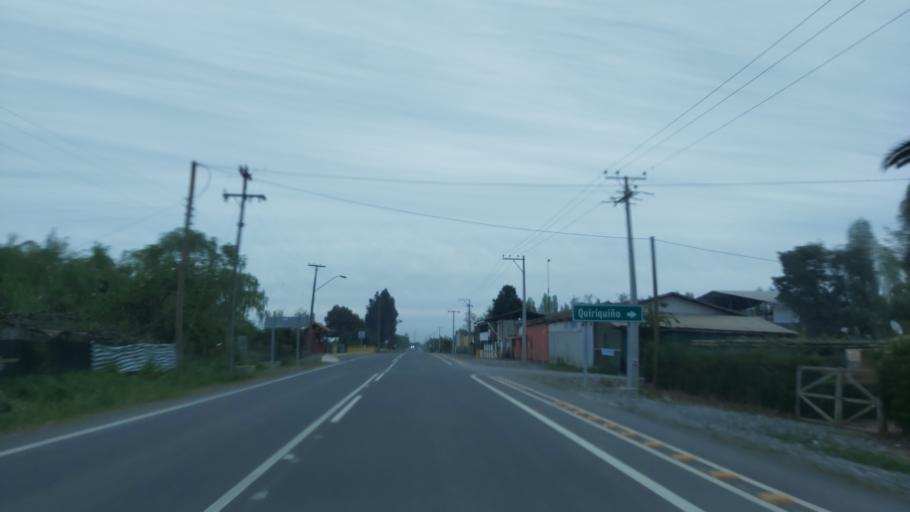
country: CL
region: Maule
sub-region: Provincia de Linares
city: Colbun
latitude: -35.6887
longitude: -71.4793
